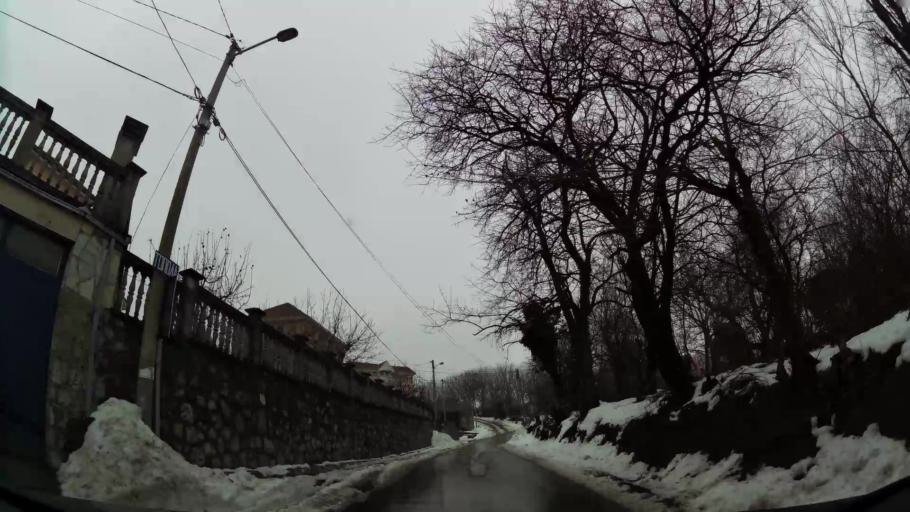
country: RS
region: Central Serbia
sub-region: Belgrade
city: Zvezdara
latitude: 44.7472
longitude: 20.5103
